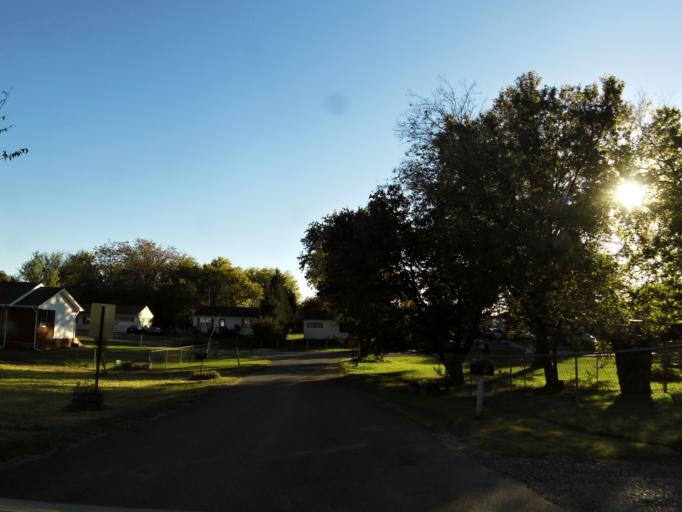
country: US
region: Tennessee
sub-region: Blount County
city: Alcoa
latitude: 35.7897
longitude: -83.9543
